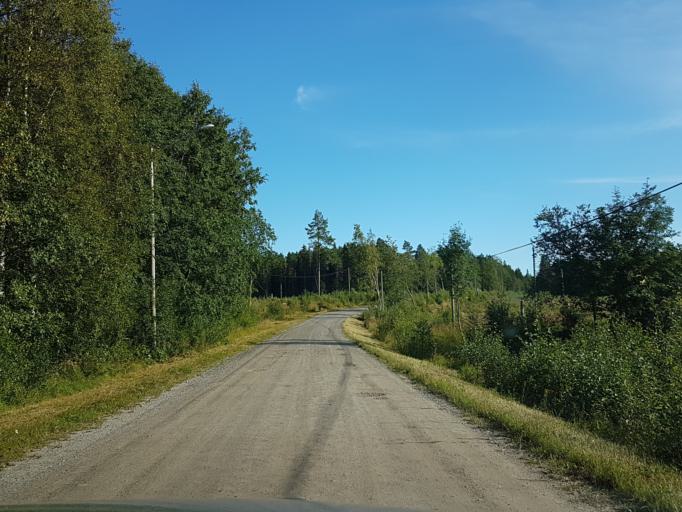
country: SE
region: Vaesterbotten
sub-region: Robertsfors Kommun
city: Robertsfors
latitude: 64.0573
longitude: 20.8694
